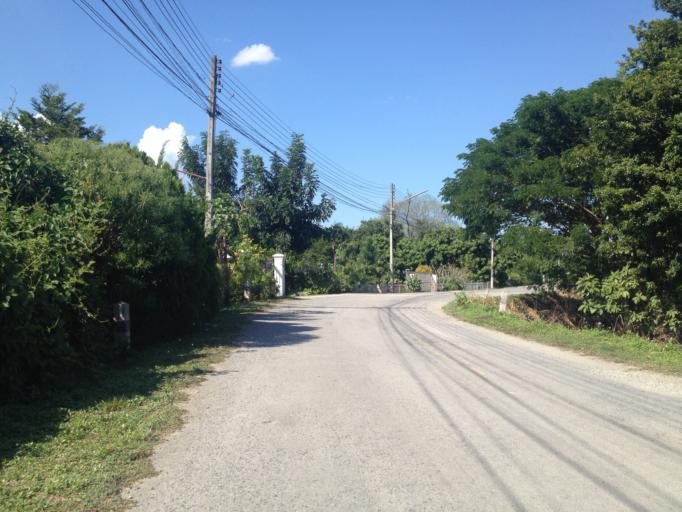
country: TH
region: Chiang Mai
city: Saraphi
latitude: 18.6809
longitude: 98.9860
